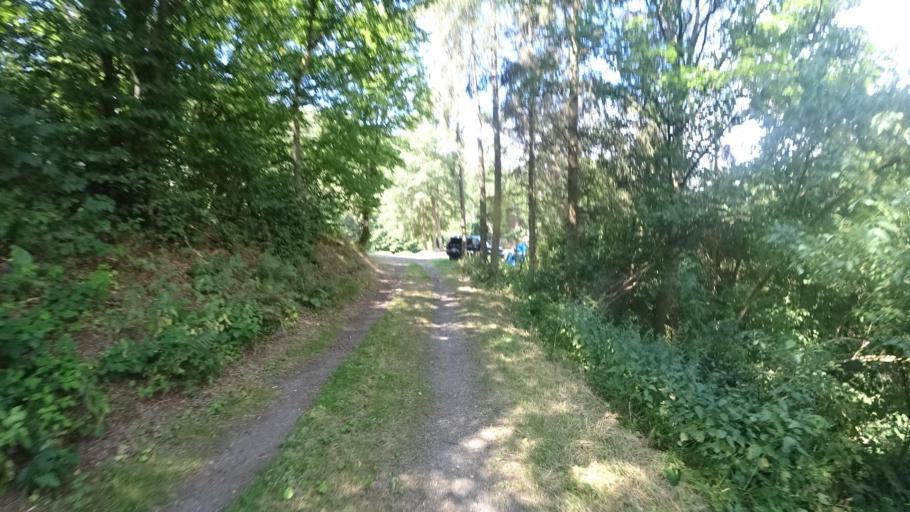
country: DE
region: Rheinland-Pfalz
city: Heckenbach
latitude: 50.4783
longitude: 7.0446
